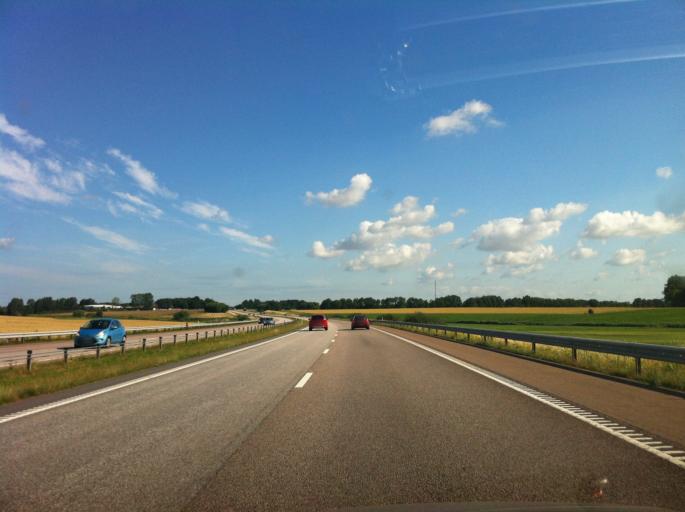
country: SE
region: Skane
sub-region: Angelholms Kommun
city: Strovelstorp
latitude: 56.1445
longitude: 12.8441
